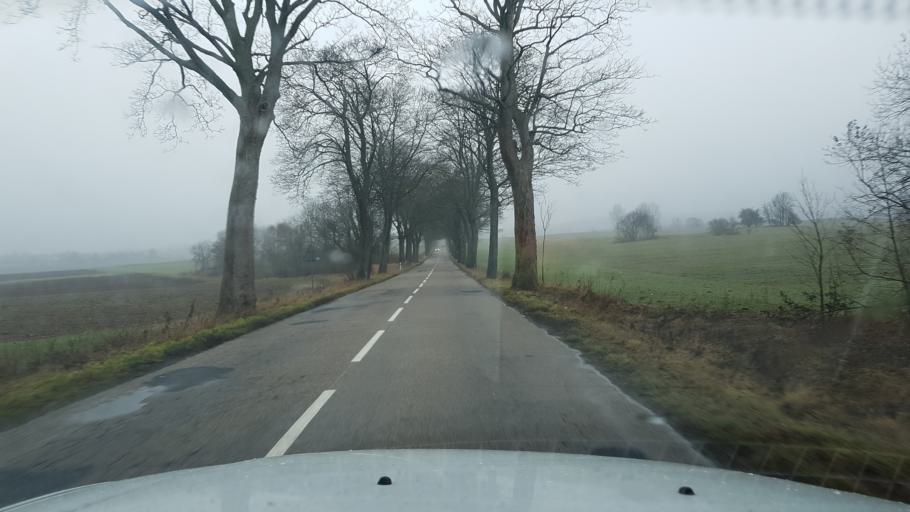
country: PL
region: West Pomeranian Voivodeship
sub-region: Powiat drawski
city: Czaplinek
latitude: 53.5744
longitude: 16.2340
